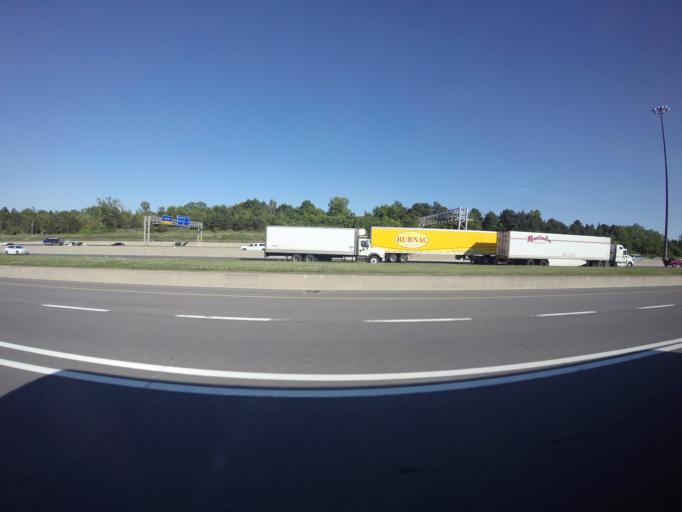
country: CA
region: Ontario
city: Pickering
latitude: 43.8007
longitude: -79.1409
